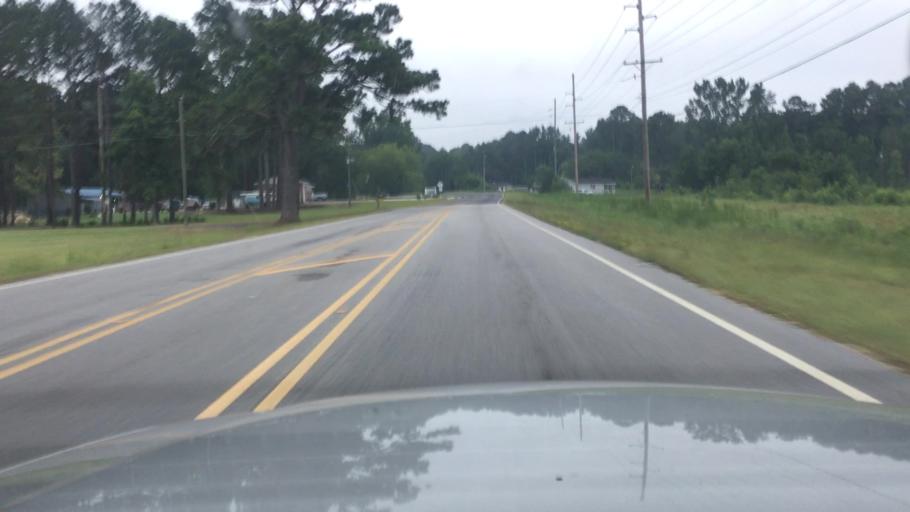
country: US
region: North Carolina
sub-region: Cumberland County
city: Fayetteville
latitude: 35.0094
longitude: -78.8636
